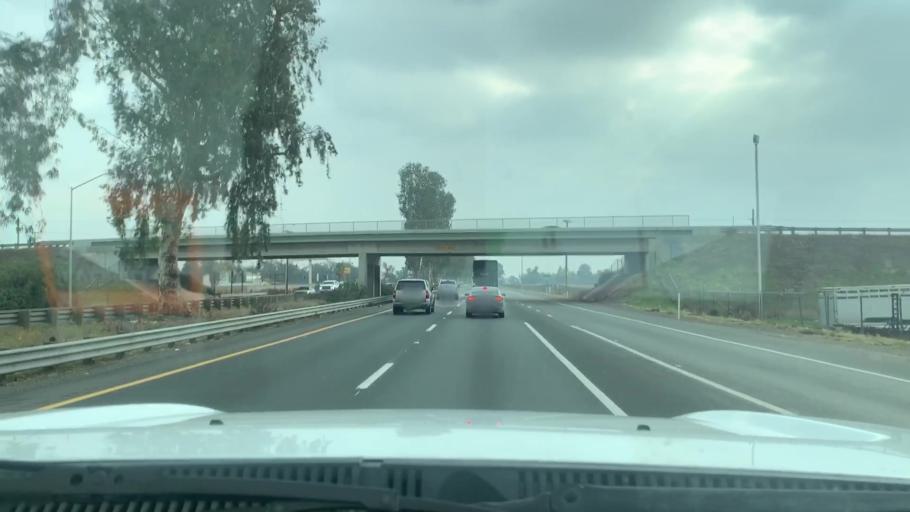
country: US
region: California
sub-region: Tulare County
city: Tulare
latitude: 36.1517
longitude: -119.3314
